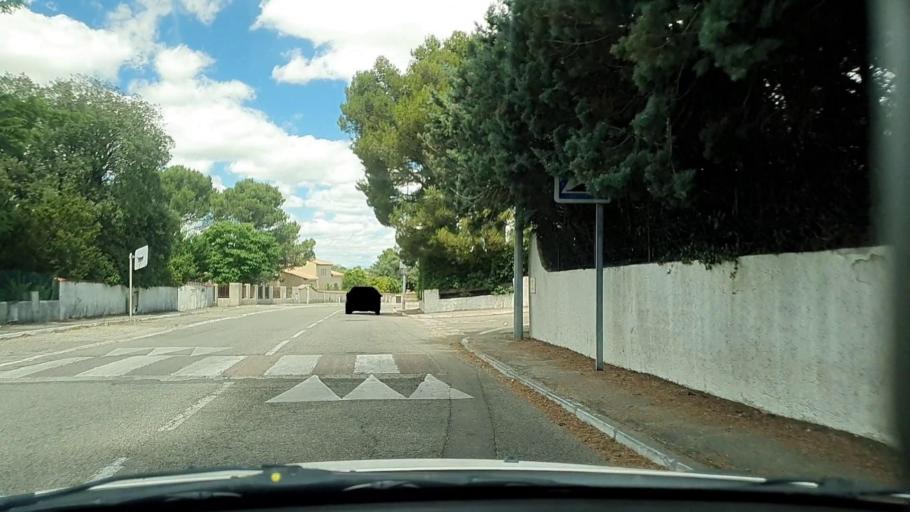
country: FR
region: Languedoc-Roussillon
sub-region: Departement du Gard
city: Poulx
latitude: 43.9063
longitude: 4.4214
